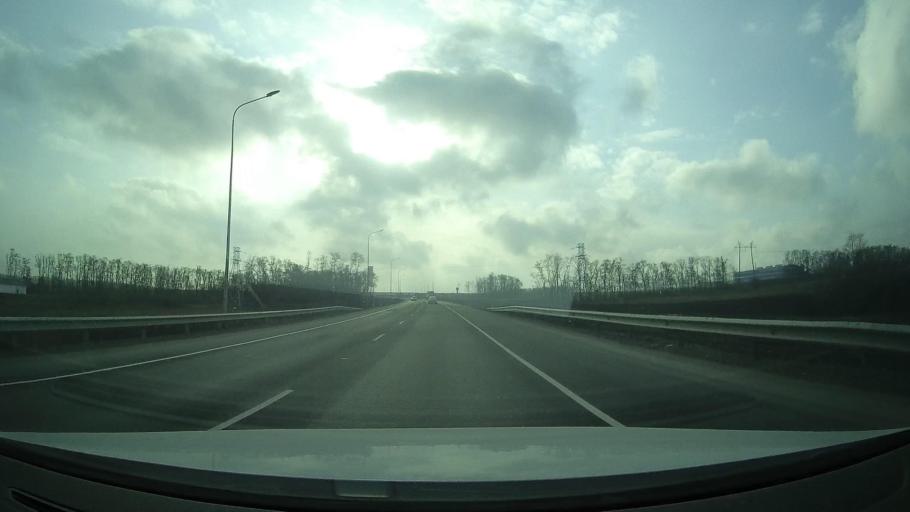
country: RU
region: Rostov
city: Grushevskaya
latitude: 47.3860
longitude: 39.8459
